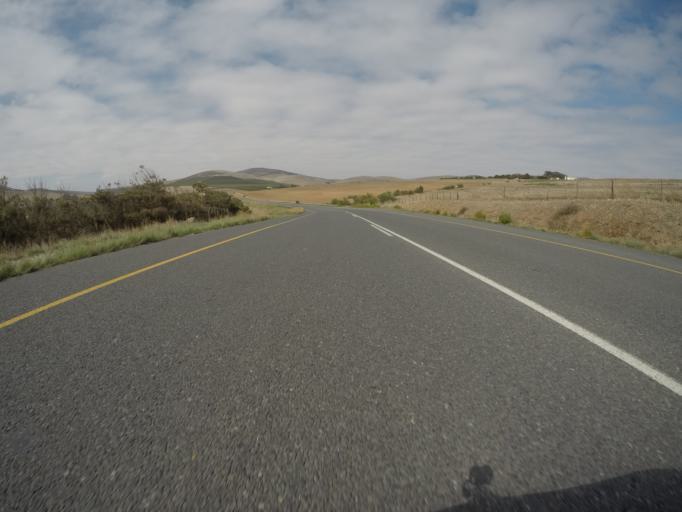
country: ZA
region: Western Cape
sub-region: City of Cape Town
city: Sunset Beach
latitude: -33.7886
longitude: 18.5758
